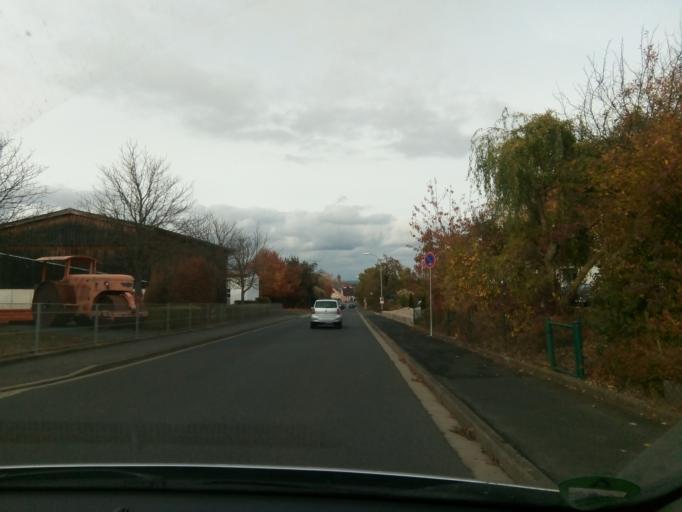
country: DE
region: Bavaria
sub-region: Regierungsbezirk Unterfranken
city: Gerolzhofen
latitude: 49.8939
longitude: 10.3526
